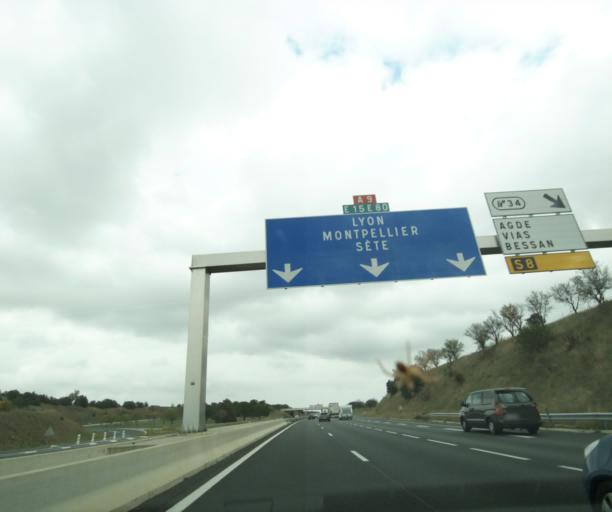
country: FR
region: Languedoc-Roussillon
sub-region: Departement de l'Herault
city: Bessan
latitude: 43.3764
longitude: 3.4119
